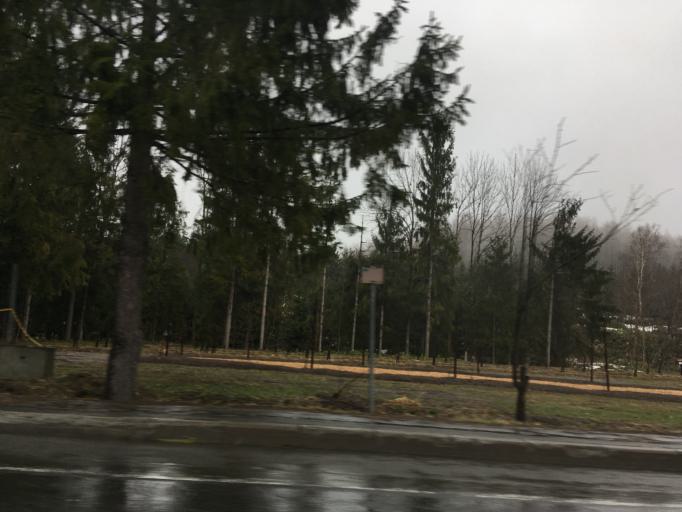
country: JP
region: Hokkaido
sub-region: Asahikawa-shi
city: Asahikawa
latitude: 43.9721
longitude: 142.4543
